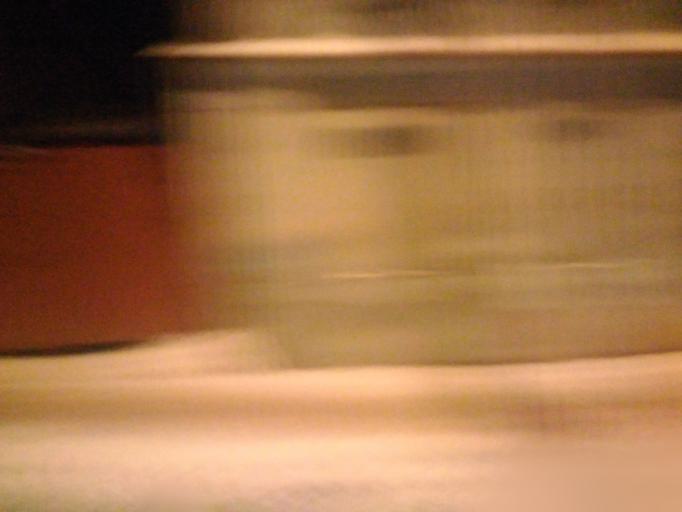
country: RU
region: Ulyanovsk
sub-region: Ulyanovskiy Rayon
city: Ulyanovsk
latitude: 54.3299
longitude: 48.4016
